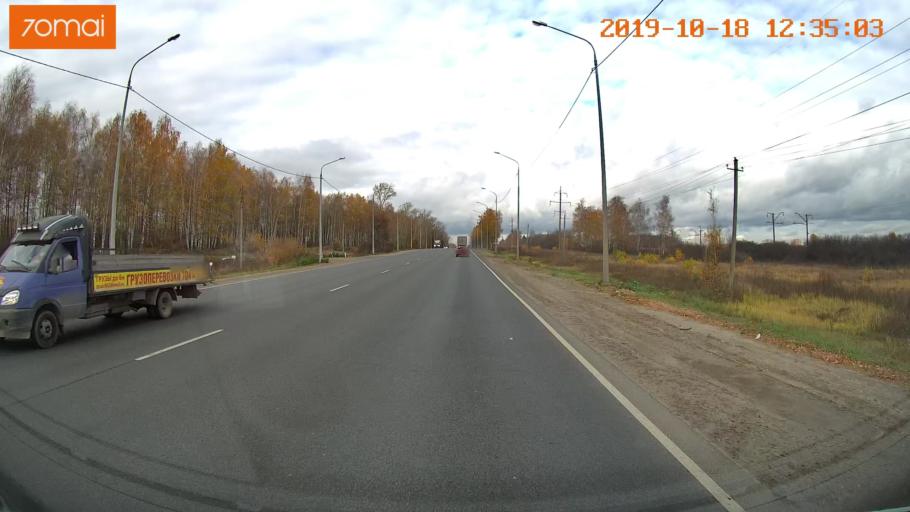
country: RU
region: Rjazan
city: Ryazan'
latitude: 54.6202
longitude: 39.6364
